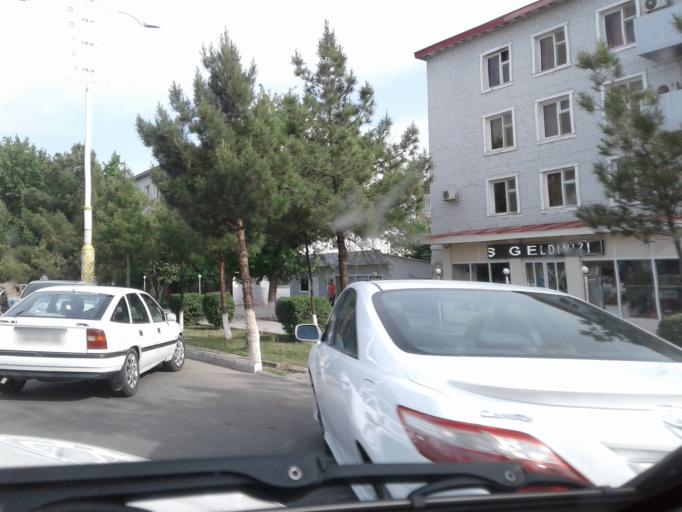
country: TM
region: Mary
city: Mary
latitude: 37.5930
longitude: 61.8420
